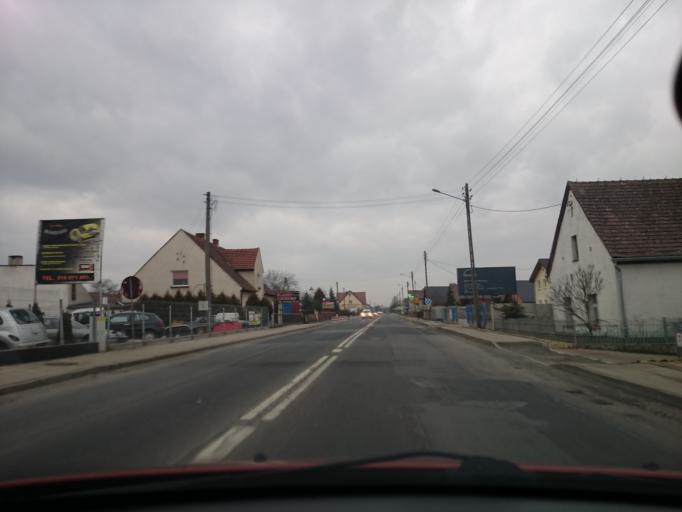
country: PL
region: Opole Voivodeship
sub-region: Powiat opolski
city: Chroscina
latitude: 50.6839
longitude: 17.8259
